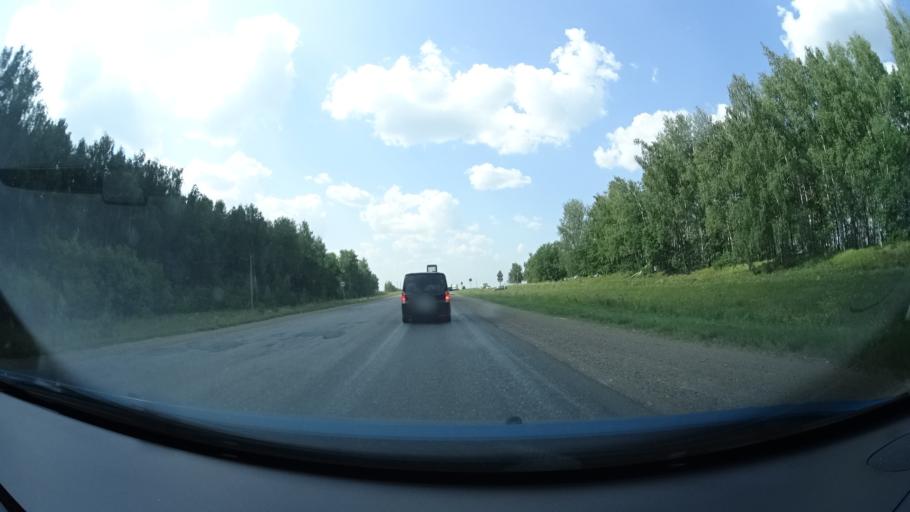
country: RU
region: Bashkortostan
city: Buzdyak
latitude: 54.6832
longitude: 54.8072
